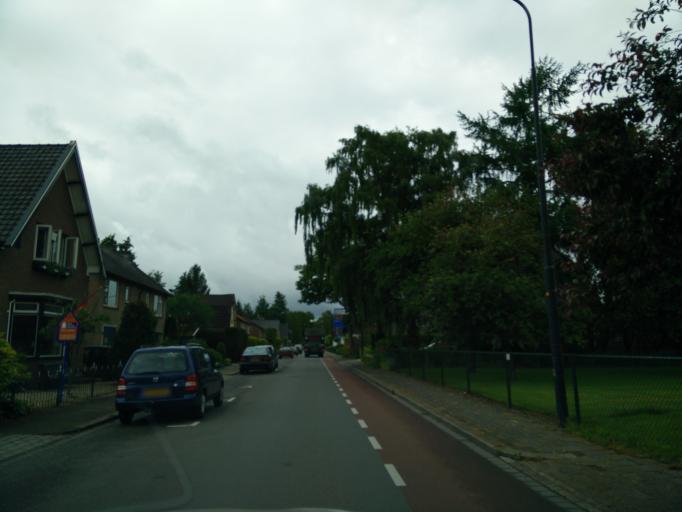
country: NL
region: Gelderland
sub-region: Gemeente Apeldoorn
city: Apeldoorn
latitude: 52.2308
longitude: 5.9574
